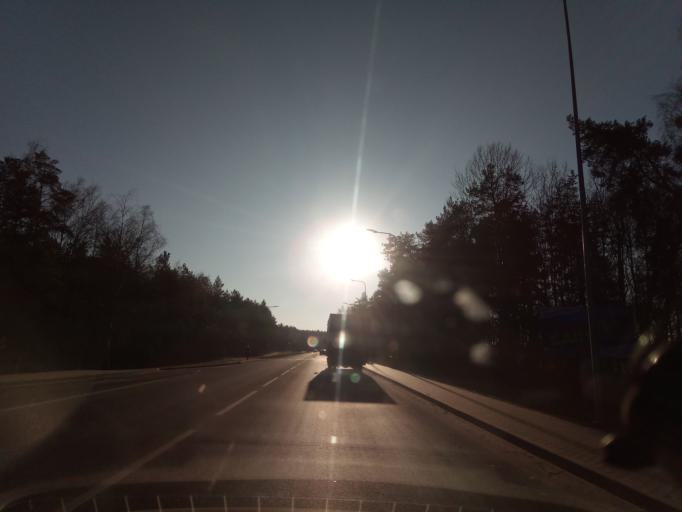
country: LT
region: Alytaus apskritis
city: Druskininkai
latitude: 54.0141
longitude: 23.9954
